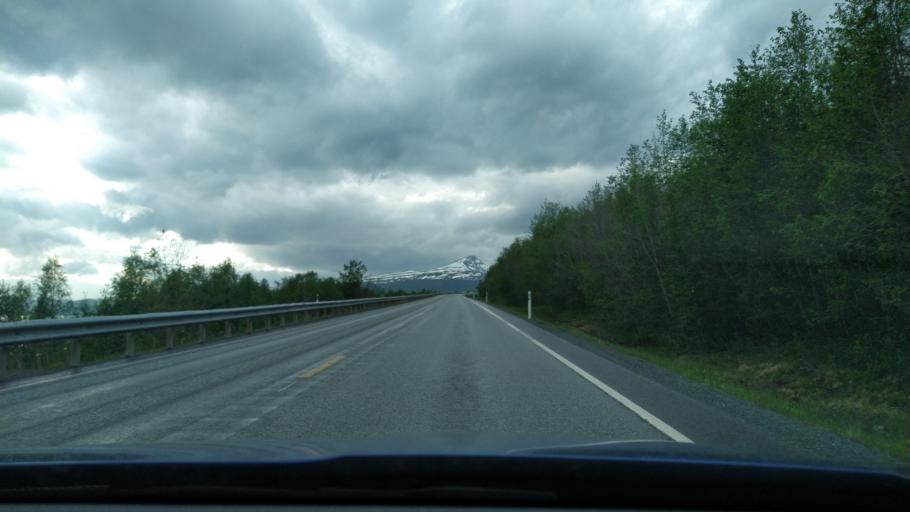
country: NO
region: Troms
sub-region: Balsfjord
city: Storsteinnes
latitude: 69.2397
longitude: 19.4654
